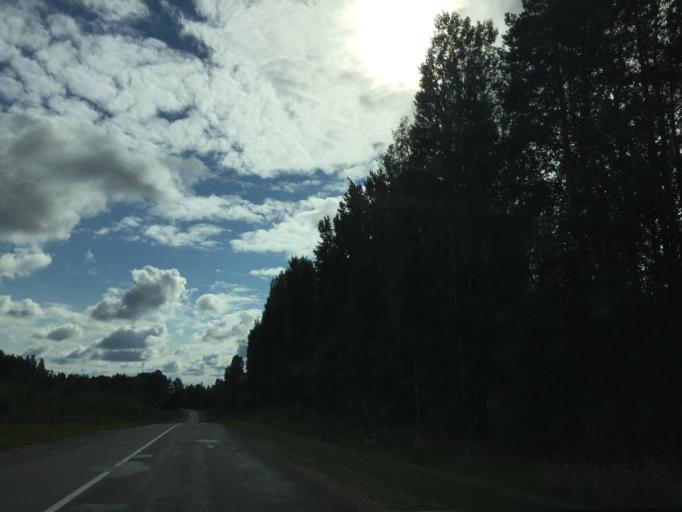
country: LV
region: Limbazu Rajons
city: Limbazi
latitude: 57.4111
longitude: 24.6948
